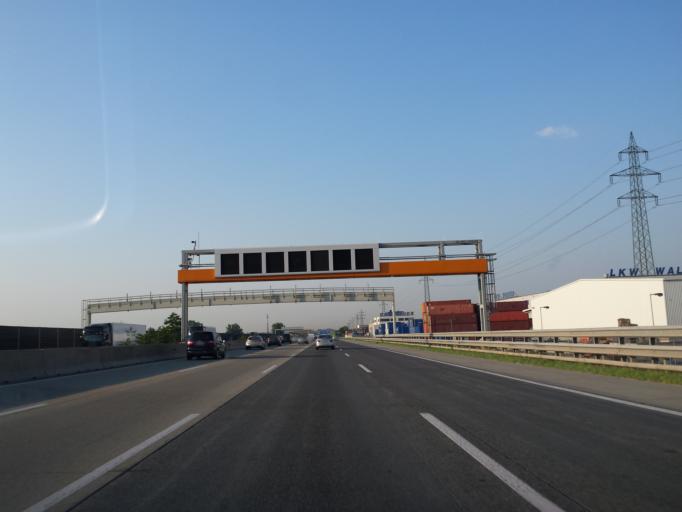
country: AT
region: Lower Austria
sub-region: Politischer Bezirk Modling
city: Biedermannsdorf
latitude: 48.0708
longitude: 16.3382
